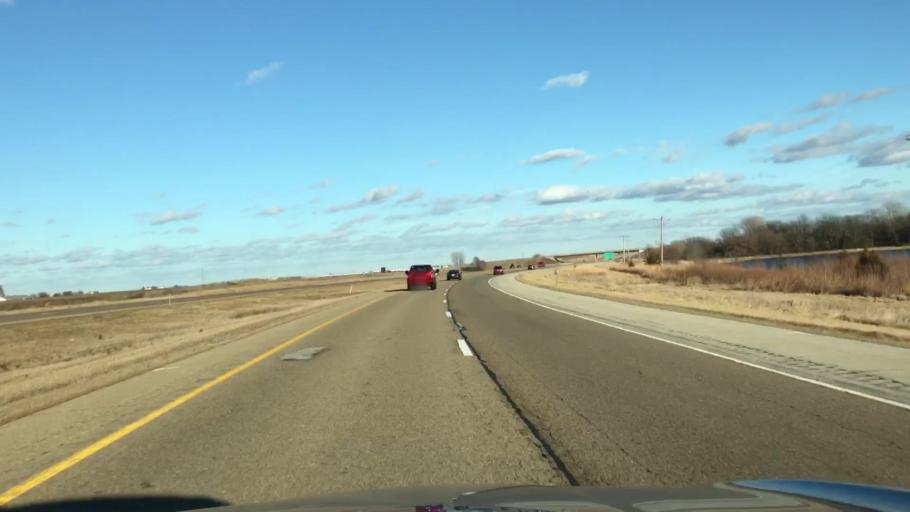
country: US
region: Illinois
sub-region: McLean County
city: Lexington
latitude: 40.6558
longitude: -88.8007
